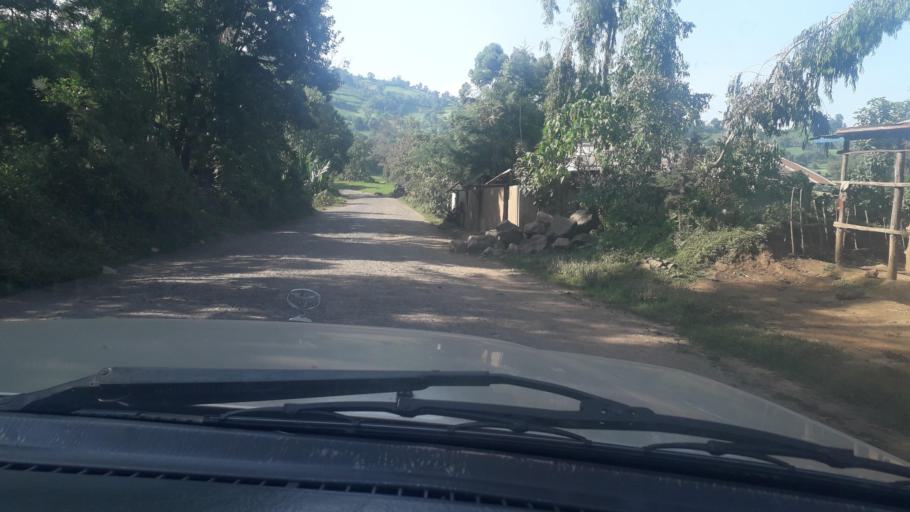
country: ET
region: Oromiya
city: Jima
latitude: 7.3835
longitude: 36.8680
